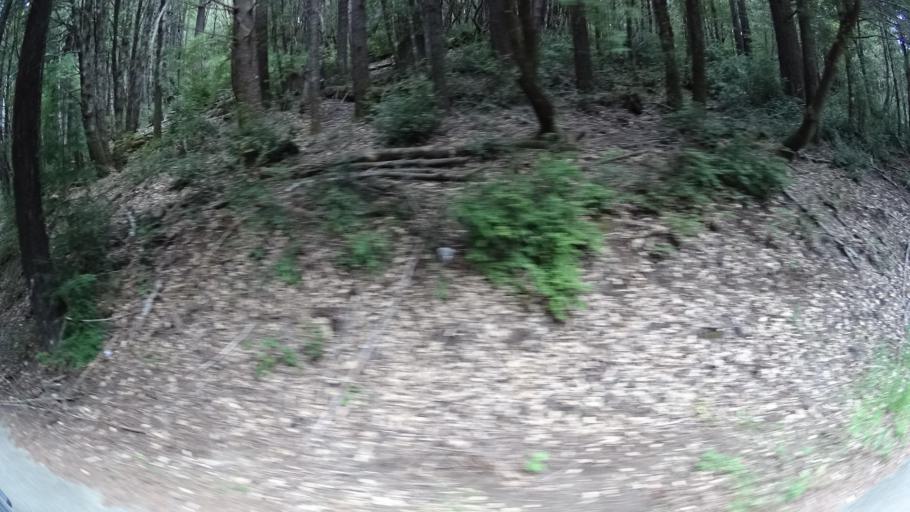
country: US
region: California
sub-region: Humboldt County
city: Redway
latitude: 40.0247
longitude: -123.9449
